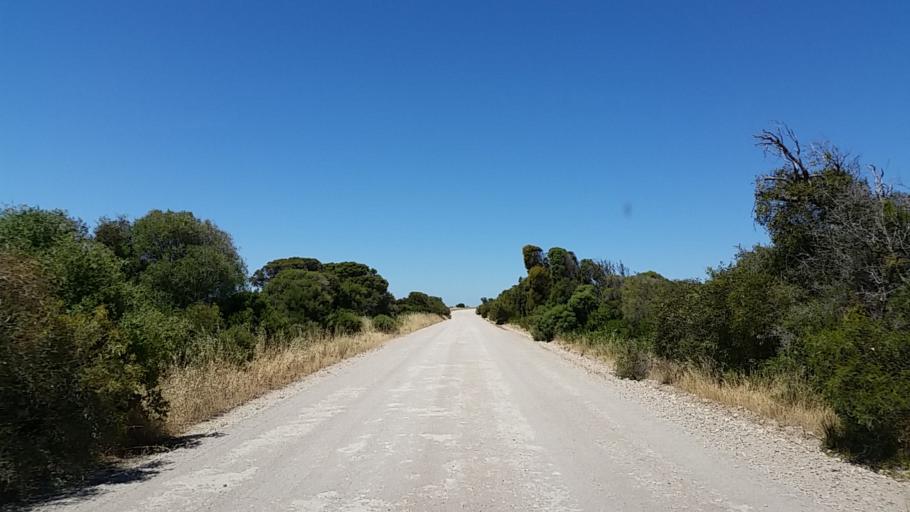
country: AU
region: South Australia
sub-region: Yorke Peninsula
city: Honiton
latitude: -35.0918
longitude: 137.4494
